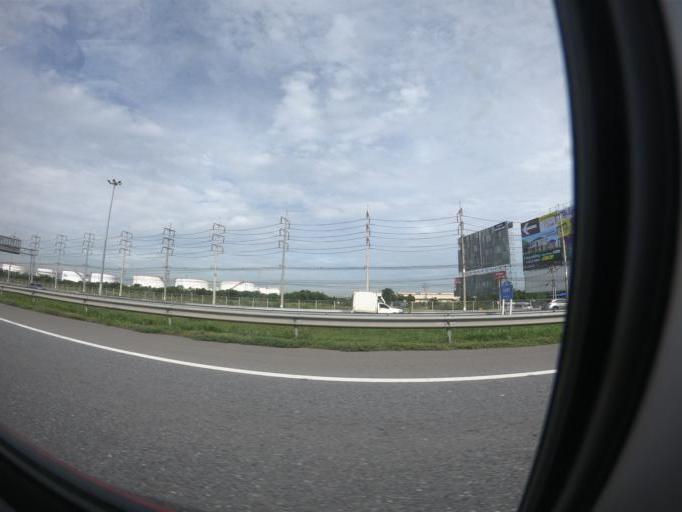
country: TH
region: Pathum Thani
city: Lam Luk Ka
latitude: 13.9292
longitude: 100.7070
